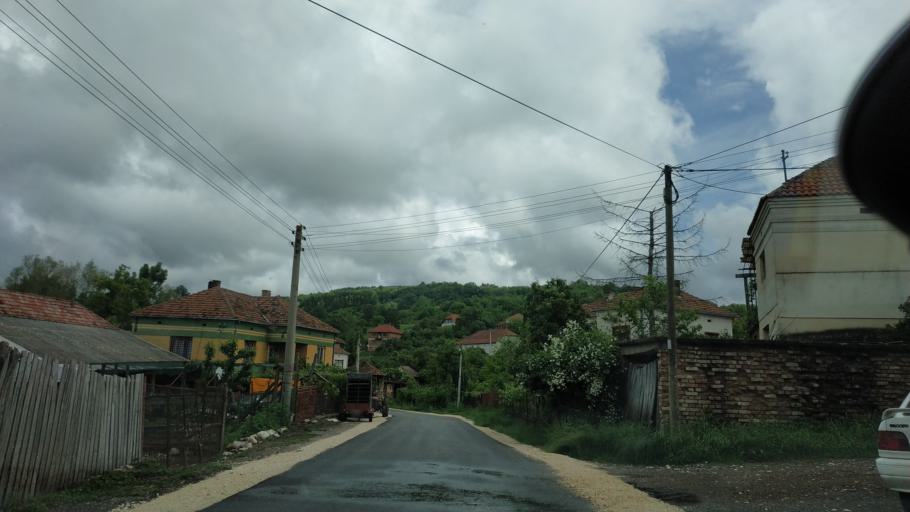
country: RS
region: Central Serbia
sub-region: Zajecarski Okrug
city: Soko Banja
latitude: 43.6776
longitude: 21.9152
